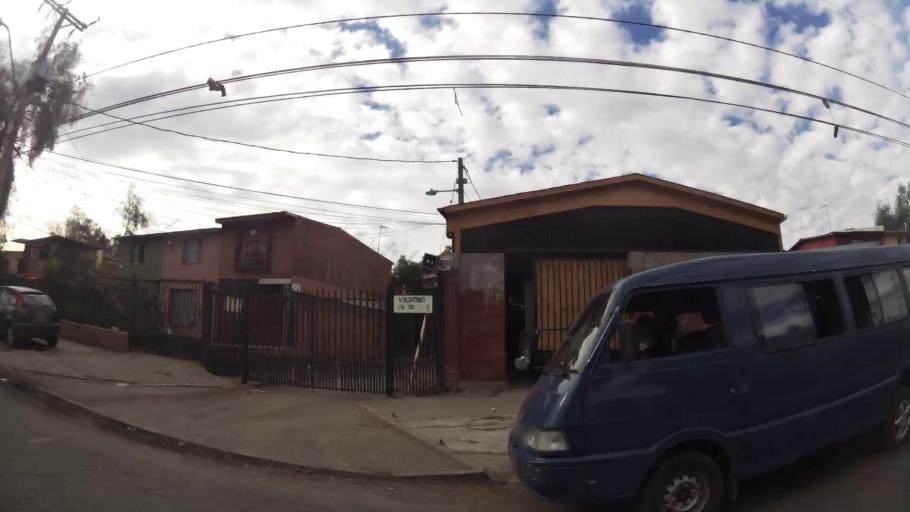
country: CL
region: Santiago Metropolitan
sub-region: Provincia de Santiago
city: La Pintana
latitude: -33.6219
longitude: -70.6169
